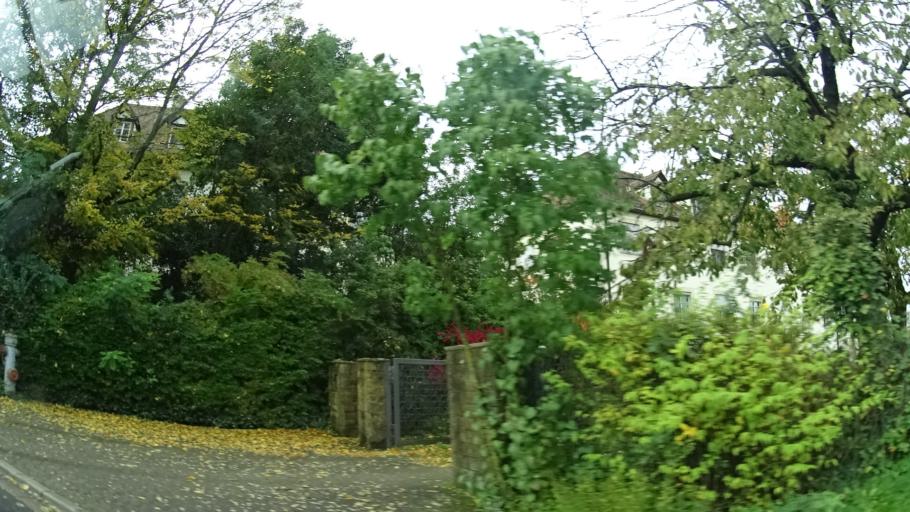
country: DE
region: Bavaria
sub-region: Upper Franconia
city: Zapfendorf
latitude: 50.0130
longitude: 10.9767
